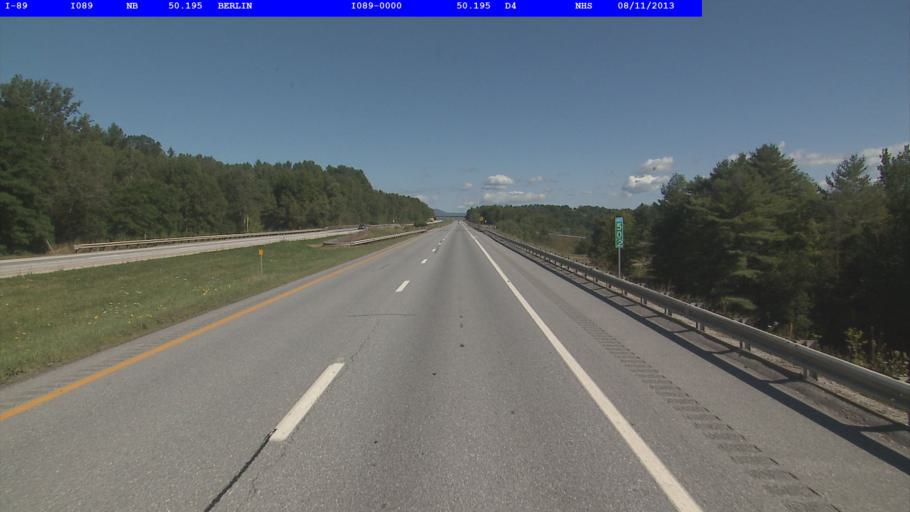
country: US
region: Vermont
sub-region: Washington County
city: Montpelier
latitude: 44.2142
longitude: -72.5833
